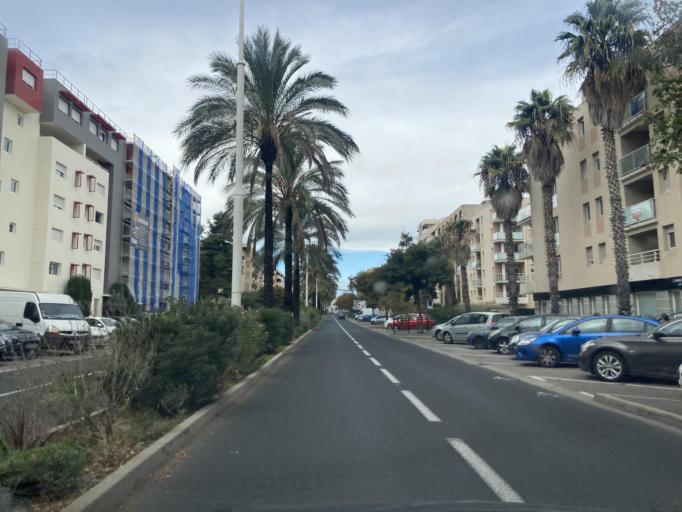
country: FR
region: Languedoc-Roussillon
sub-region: Departement des Pyrenees-Orientales
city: Perpignan
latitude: 42.6879
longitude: 2.9052
